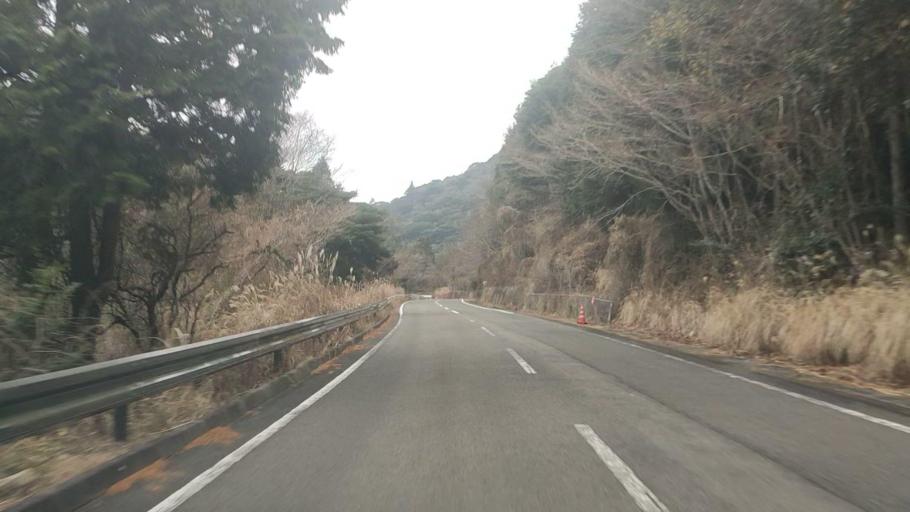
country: JP
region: Nagasaki
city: Shimabara
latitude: 32.7839
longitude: 130.2783
